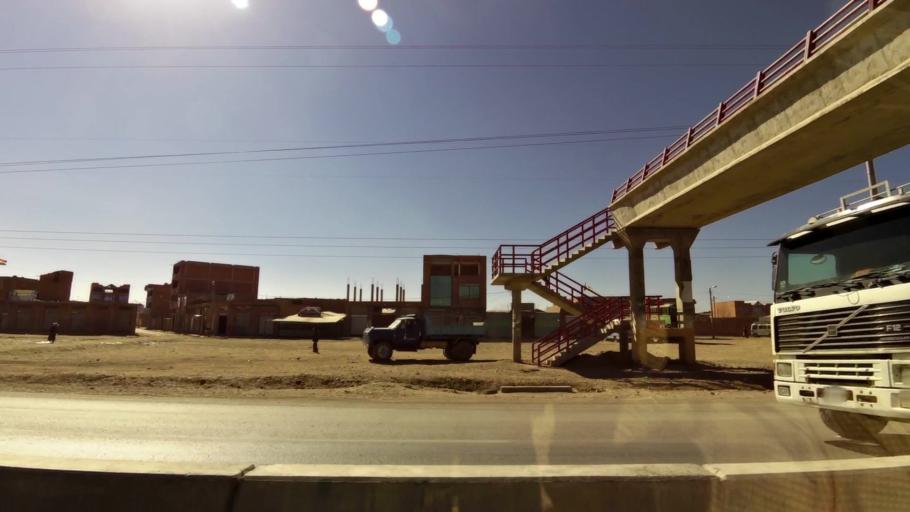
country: BO
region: La Paz
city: La Paz
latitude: -16.6132
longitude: -68.1829
